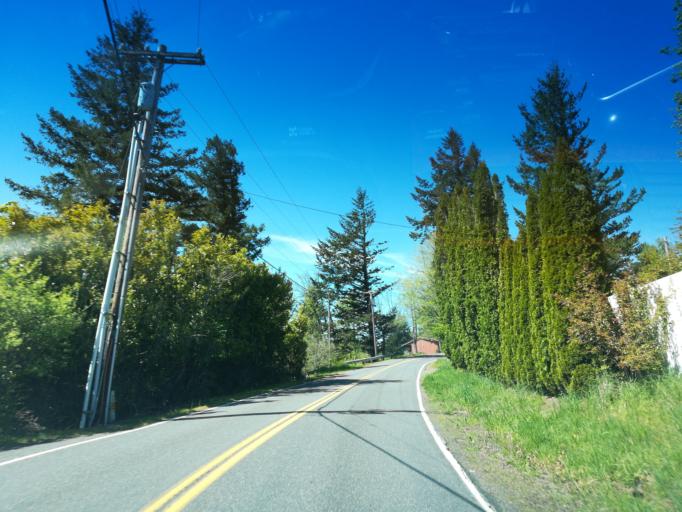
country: US
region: Oregon
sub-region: Multnomah County
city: Troutdale
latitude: 45.5205
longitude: -122.3516
